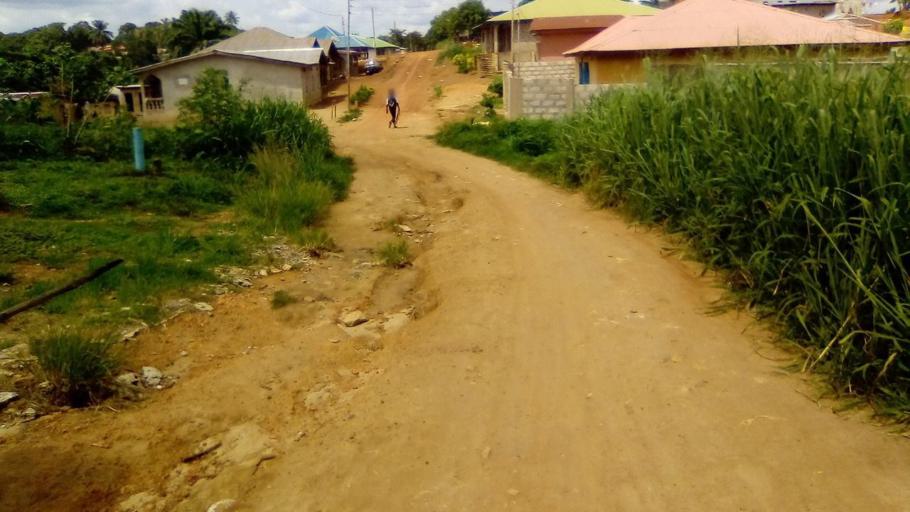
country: SL
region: Southern Province
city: Bo
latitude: 7.9667
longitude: -11.7217
